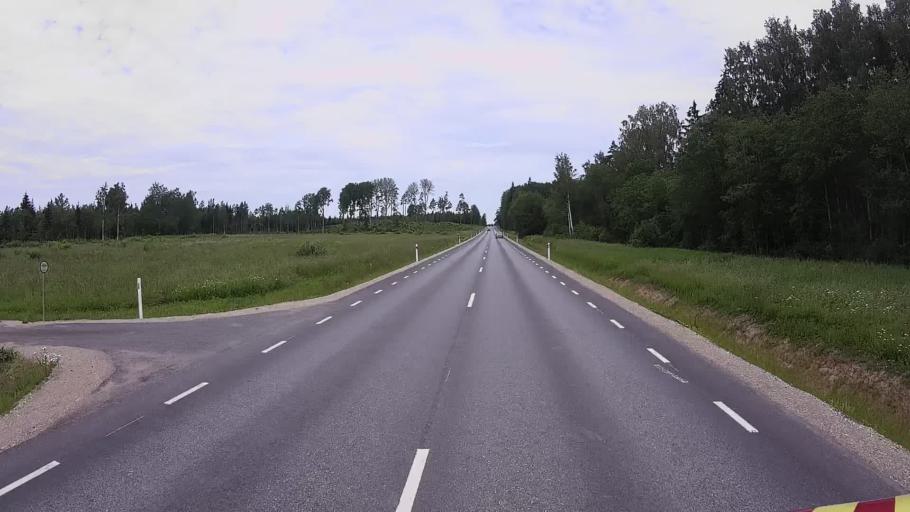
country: EE
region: Viljandimaa
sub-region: Viljandi linn
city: Viljandi
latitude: 58.2527
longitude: 25.5903
